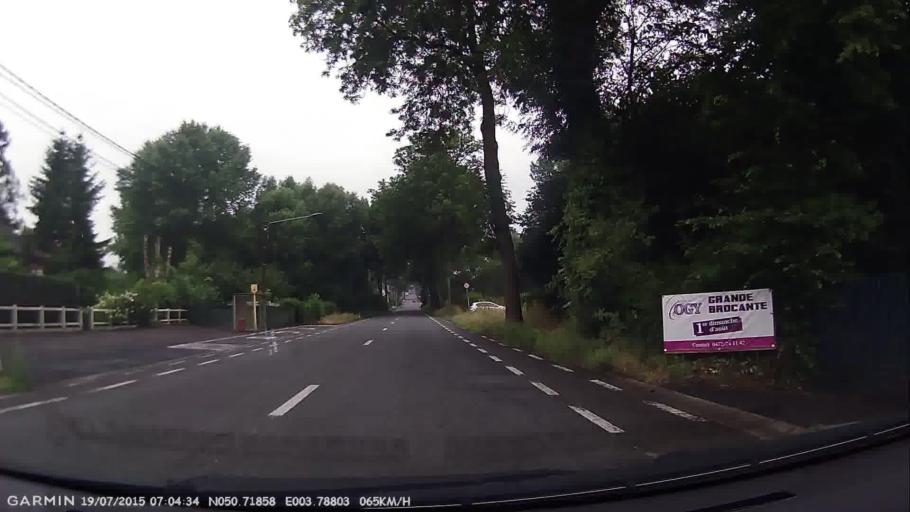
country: BE
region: Wallonia
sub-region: Province du Hainaut
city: Lessines
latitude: 50.7186
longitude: 3.7878
